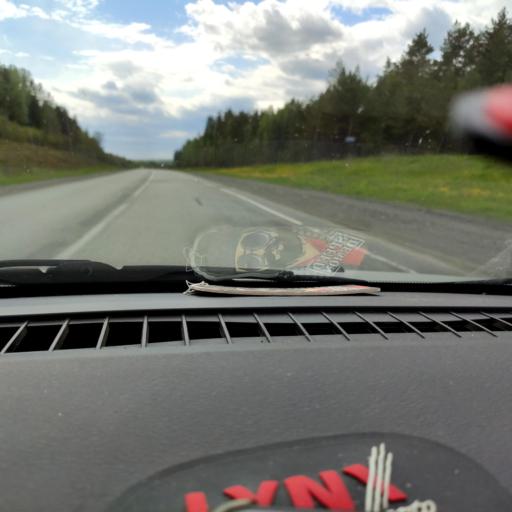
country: RU
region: Sverdlovsk
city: Druzhinino
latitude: 56.8179
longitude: 59.5643
